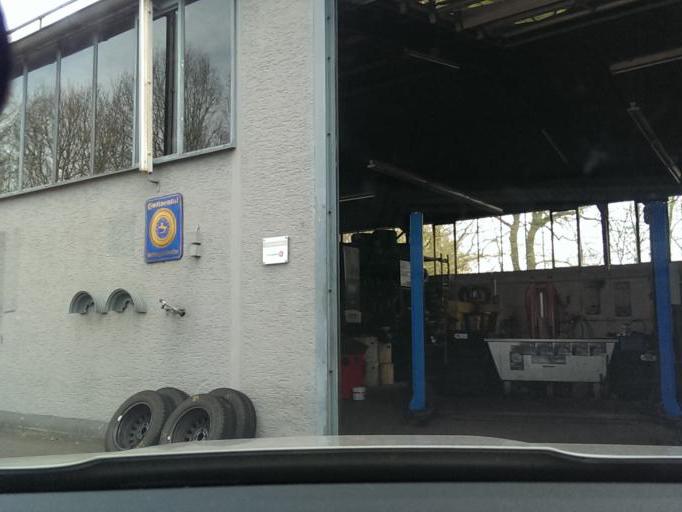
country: DE
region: North Rhine-Westphalia
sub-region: Regierungsbezirk Detmold
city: Delbruck
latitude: 51.7610
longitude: 8.5677
